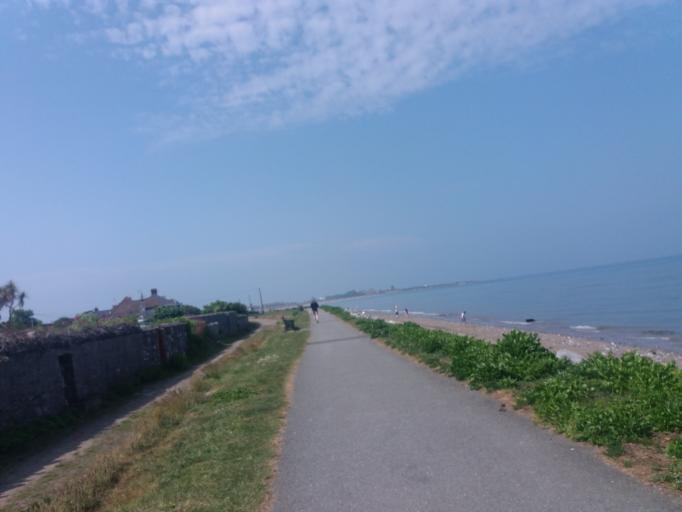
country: IE
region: Leinster
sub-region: Fingal County
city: Skerries
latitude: 53.5730
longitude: -6.1012
